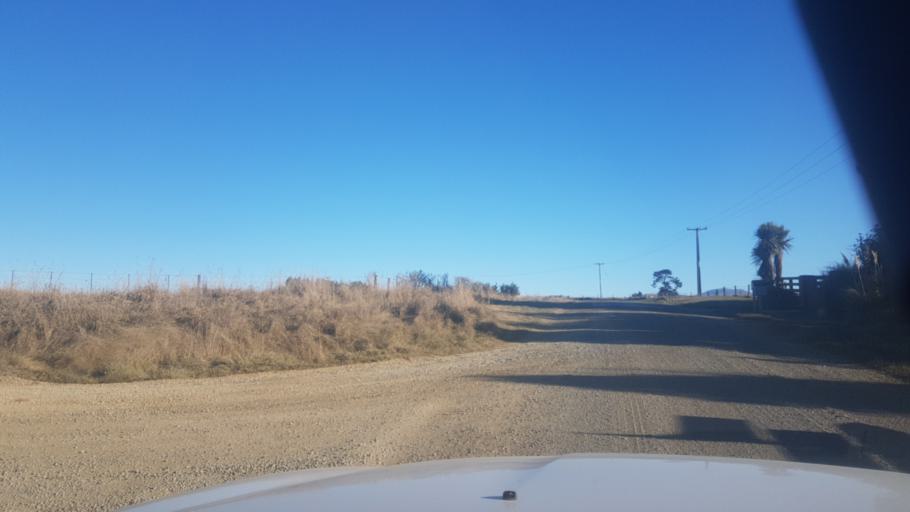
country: NZ
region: Canterbury
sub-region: Timaru District
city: Pleasant Point
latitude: -44.3463
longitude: 171.0754
